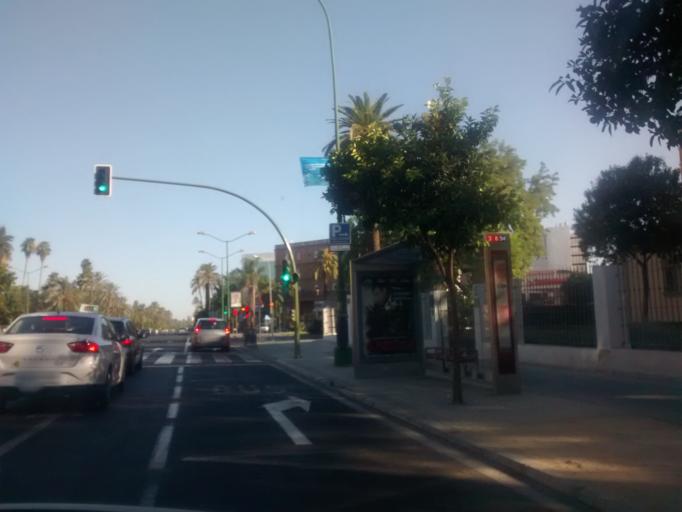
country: ES
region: Andalusia
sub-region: Provincia de Sevilla
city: Sevilla
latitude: 37.3701
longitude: -5.9884
